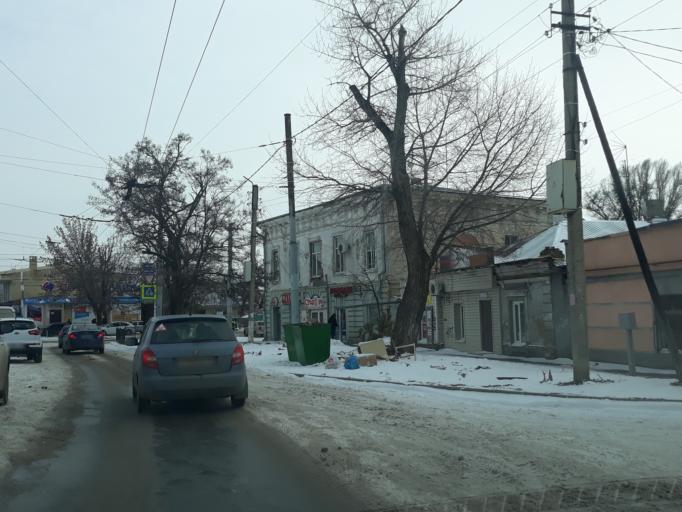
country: RU
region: Rostov
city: Taganrog
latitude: 47.2122
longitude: 38.9148
